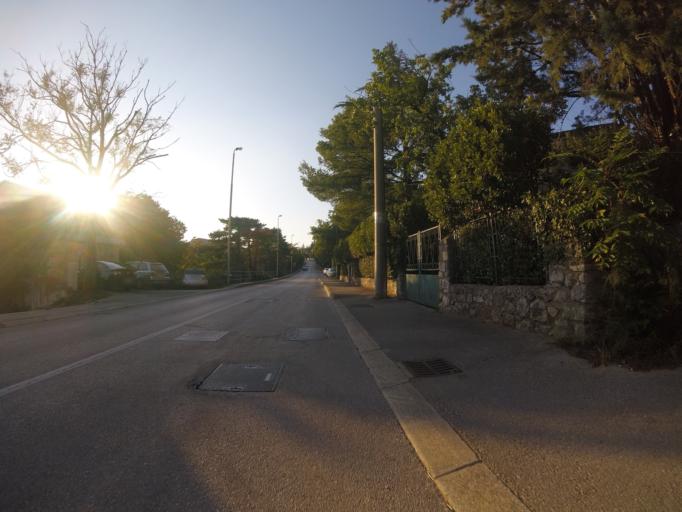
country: HR
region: Primorsko-Goranska
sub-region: Grad Crikvenica
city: Crikvenica
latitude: 45.1887
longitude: 14.6744
